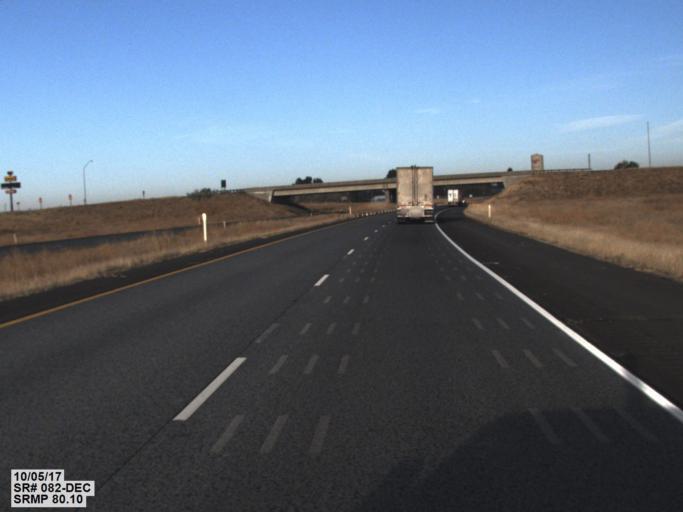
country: US
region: Washington
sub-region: Benton County
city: Prosser
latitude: 46.2219
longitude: -119.7871
